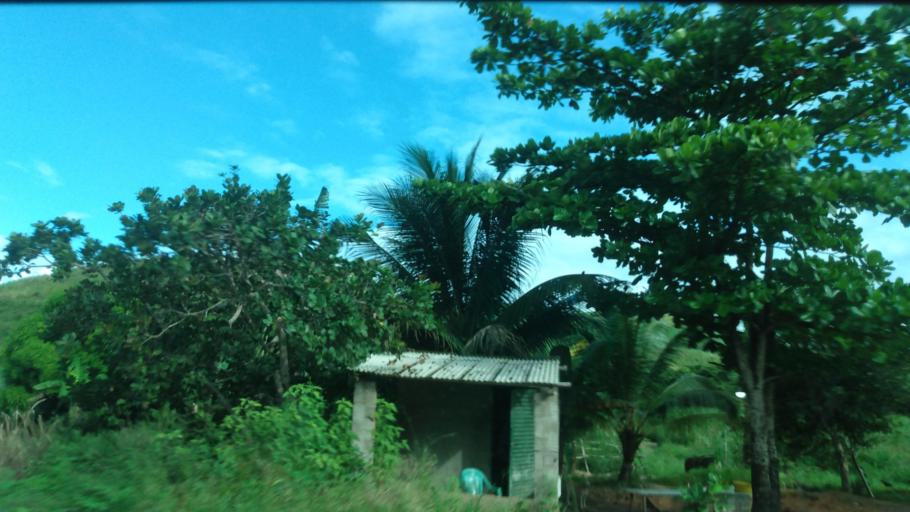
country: BR
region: Pernambuco
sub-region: Palmares
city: Palmares
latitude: -8.6922
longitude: -35.6382
